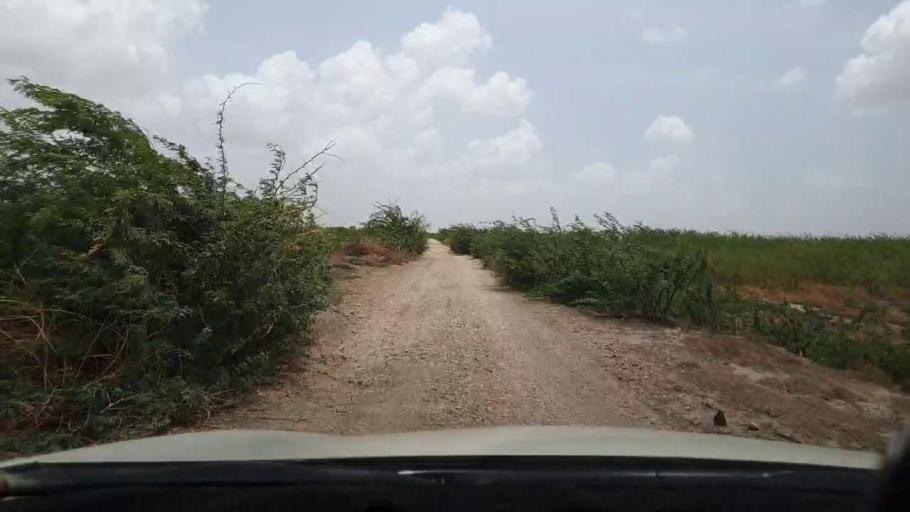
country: PK
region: Sindh
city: Kadhan
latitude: 24.3530
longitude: 68.9234
